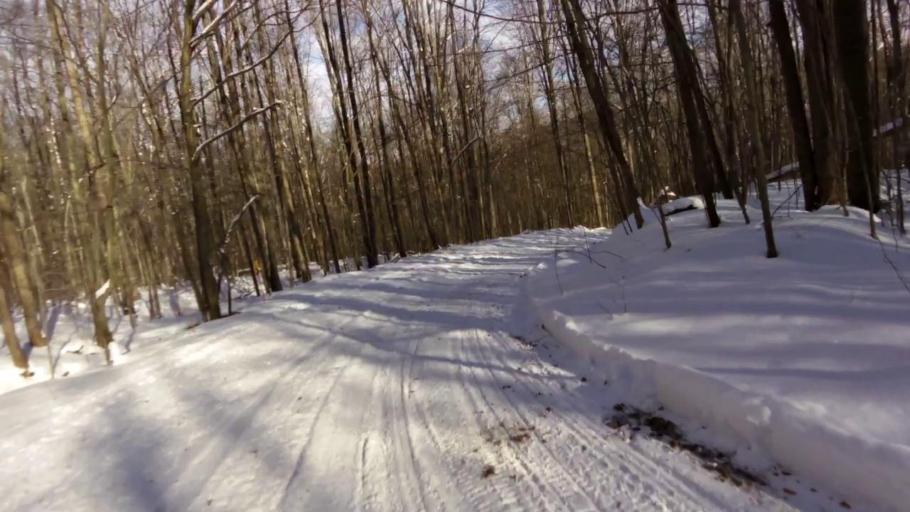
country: US
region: Pennsylvania
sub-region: McKean County
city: Foster Brook
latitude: 42.0652
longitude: -78.6566
